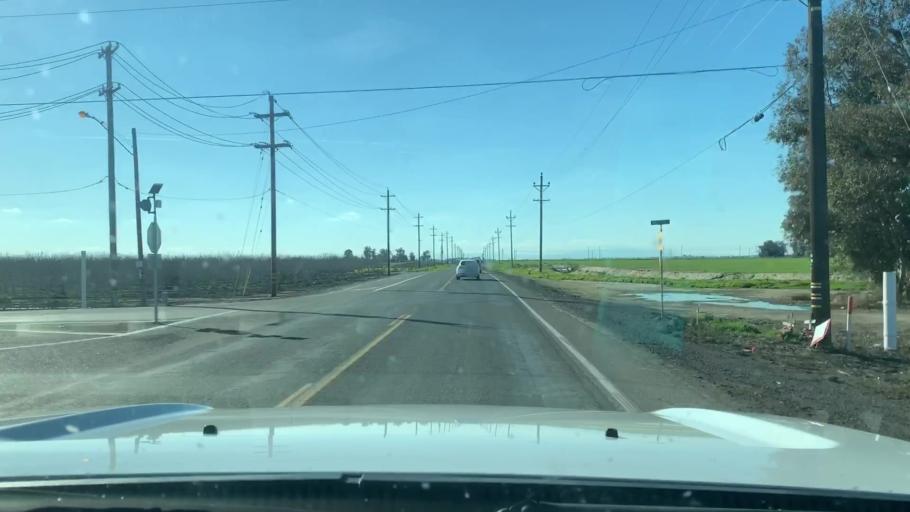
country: US
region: California
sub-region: Kings County
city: Home Garden
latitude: 36.2113
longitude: -119.6458
